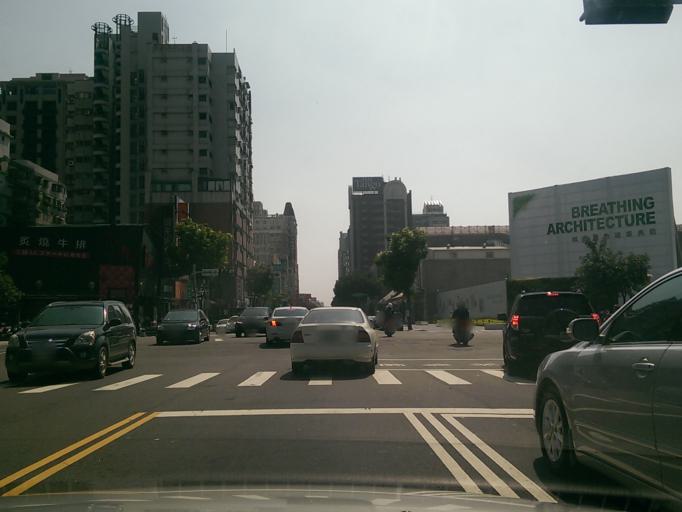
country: TW
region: Taiwan
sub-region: Taichung City
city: Taichung
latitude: 24.1513
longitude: 120.6497
